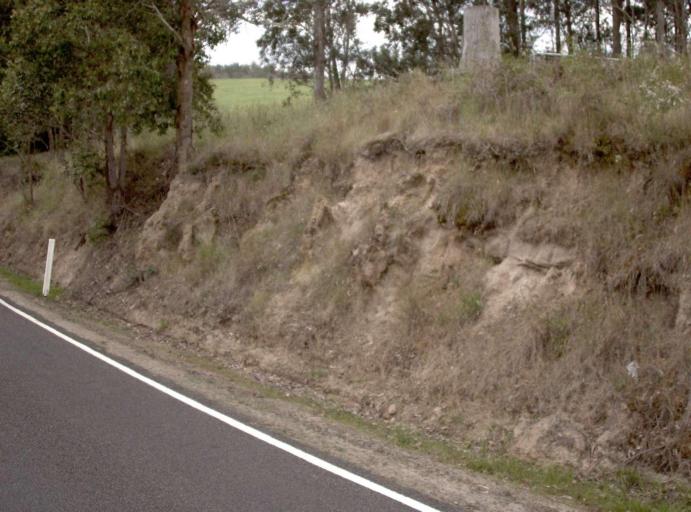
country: AU
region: New South Wales
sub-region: Bombala
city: Bombala
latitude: -37.4794
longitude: 149.1805
